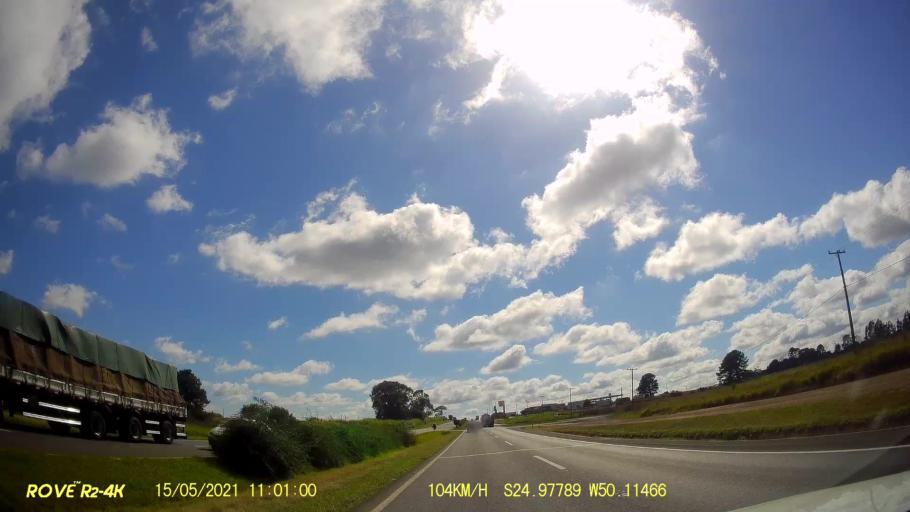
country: BR
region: Parana
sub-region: Carambei
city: Carambei
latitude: -24.9779
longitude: -50.1149
